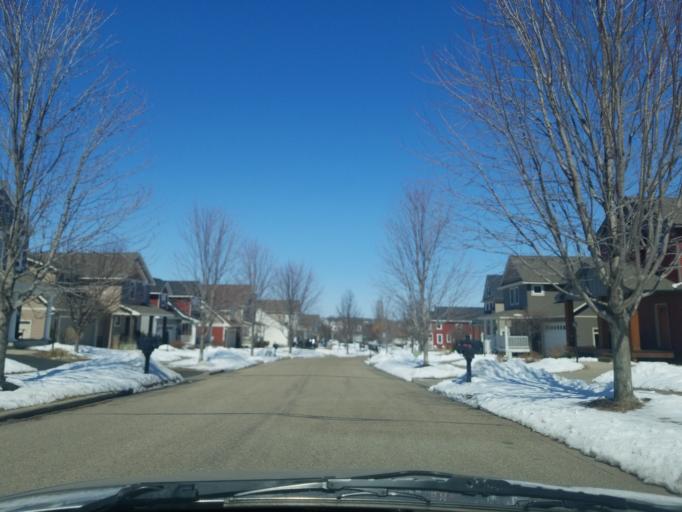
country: US
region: Wisconsin
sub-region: Saint Croix County
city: Hudson
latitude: 44.9563
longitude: -92.7000
